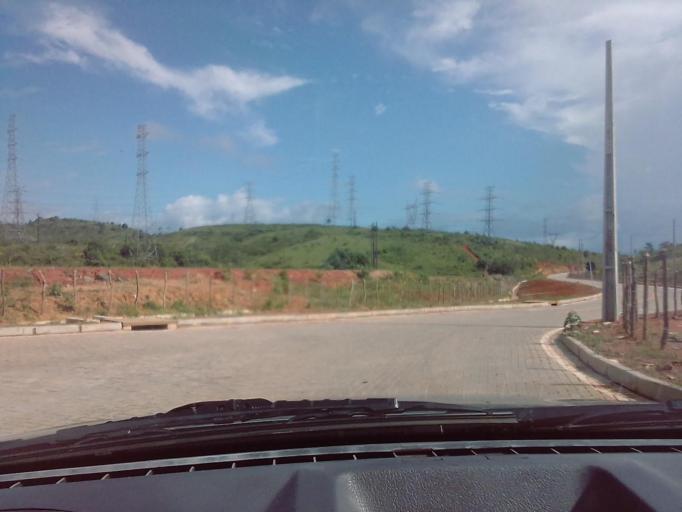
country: BR
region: Pernambuco
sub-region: Jaboatao Dos Guararapes
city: Jaboatao dos Guararapes
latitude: -8.1097
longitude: -35.0318
